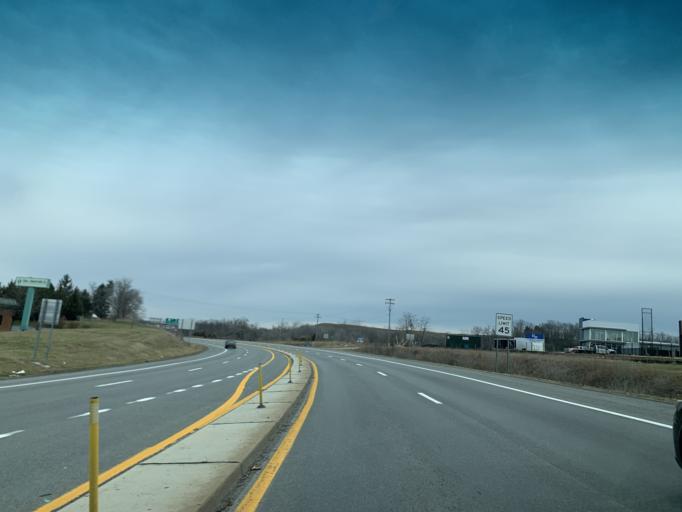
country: US
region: West Virginia
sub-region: Berkeley County
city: Martinsburg
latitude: 39.4406
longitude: -77.9773
